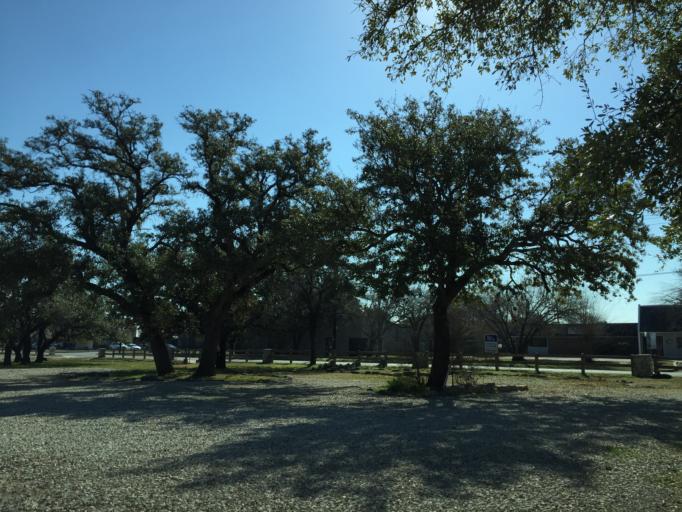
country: US
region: Texas
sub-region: Williamson County
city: Round Rock
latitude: 30.5173
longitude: -97.6967
